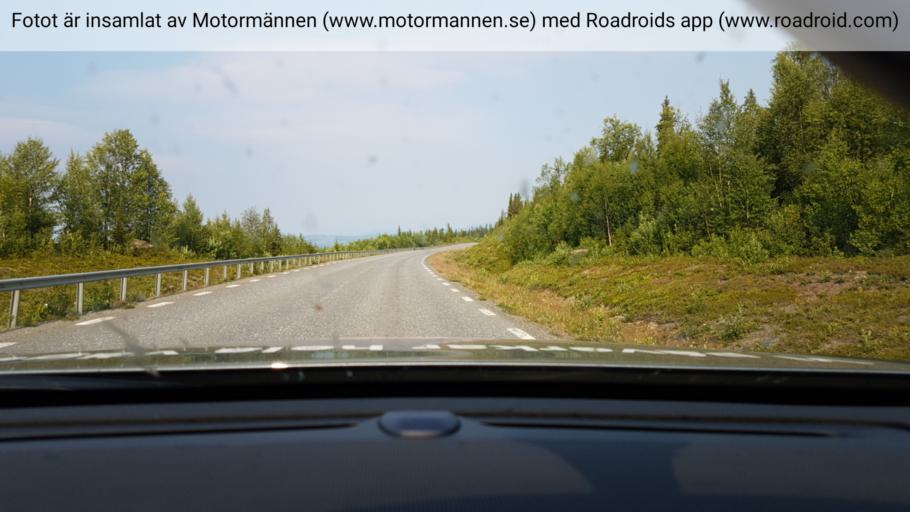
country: SE
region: Vaesterbotten
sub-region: Vilhelmina Kommun
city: Sjoberg
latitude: 65.4406
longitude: 16.1126
